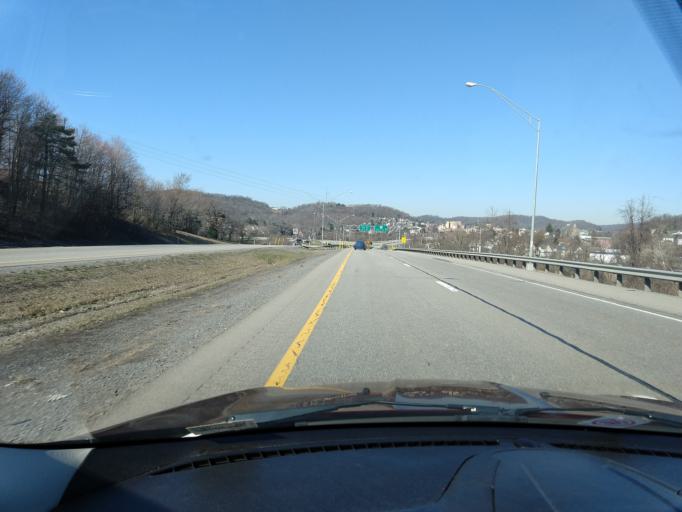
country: US
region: West Virginia
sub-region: Harrison County
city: Nutter Fort
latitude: 39.2773
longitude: -80.3153
